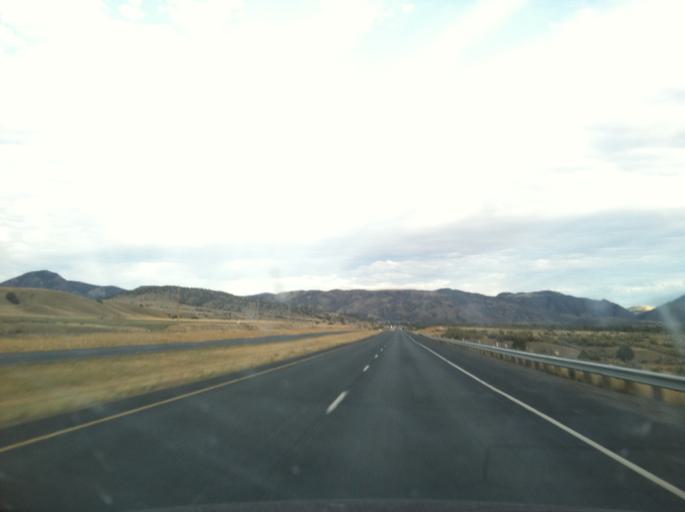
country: US
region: Montana
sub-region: Jefferson County
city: Whitehall
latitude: 45.8762
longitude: -111.9976
